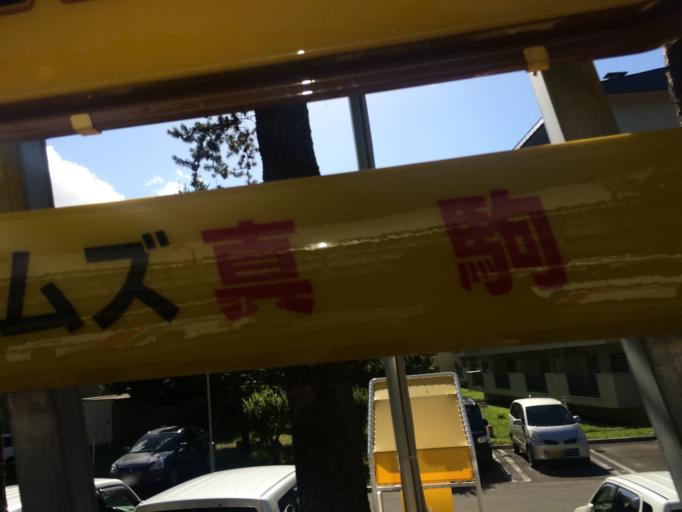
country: JP
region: Hokkaido
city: Sapporo
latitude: 42.9929
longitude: 141.3584
